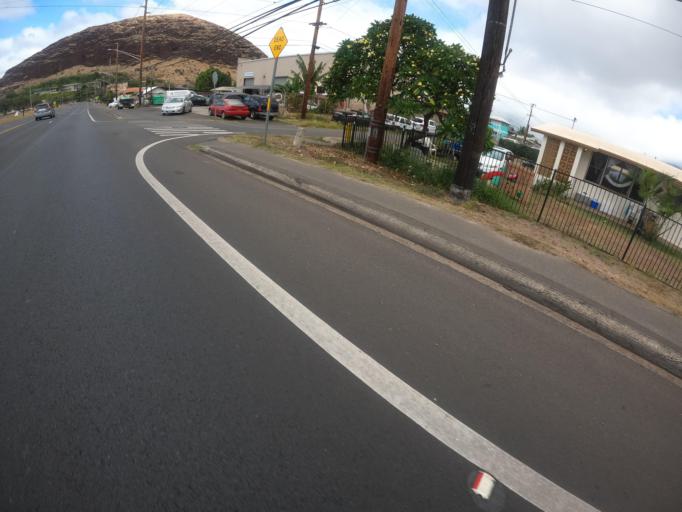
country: US
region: Hawaii
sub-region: Honolulu County
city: Ma'ili
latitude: 21.4249
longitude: -158.1781
